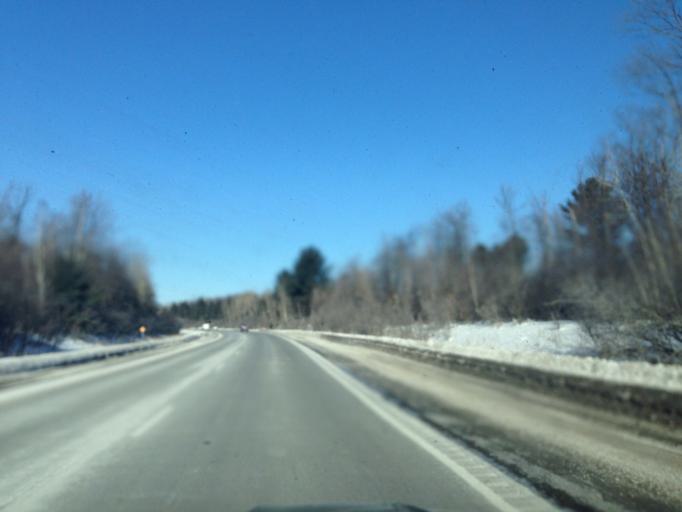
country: CA
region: Ontario
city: Ottawa
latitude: 45.3608
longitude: -75.4775
